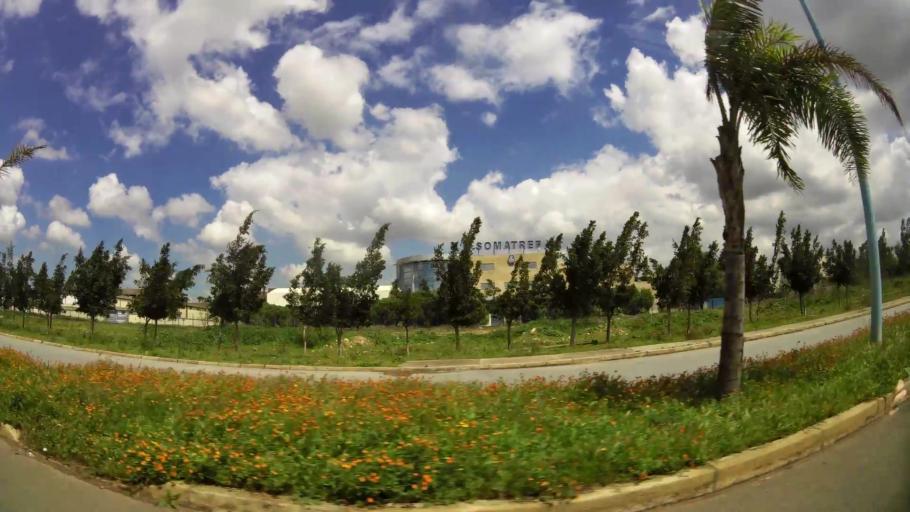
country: MA
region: Grand Casablanca
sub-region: Mediouna
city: Mediouna
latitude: 33.4028
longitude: -7.5562
